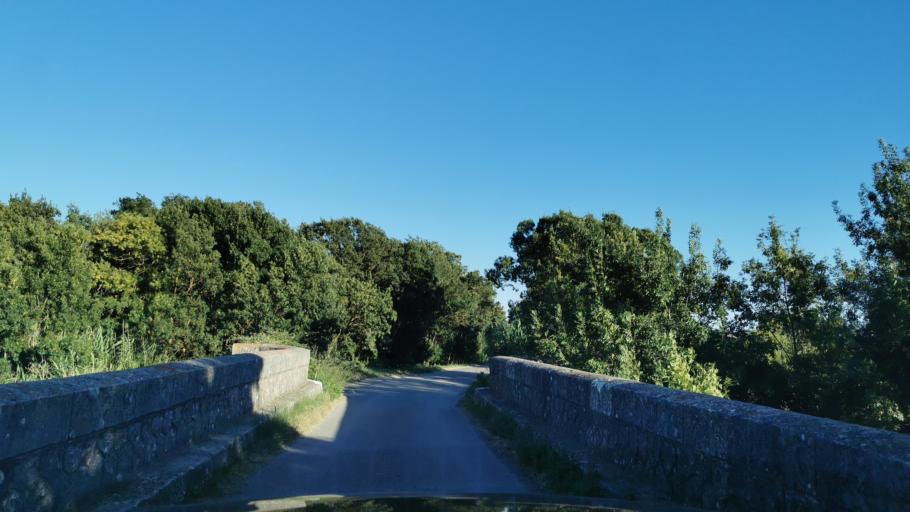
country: FR
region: Languedoc-Roussillon
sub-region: Departement de l'Aude
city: Ouveillan
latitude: 43.2615
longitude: 2.9862
